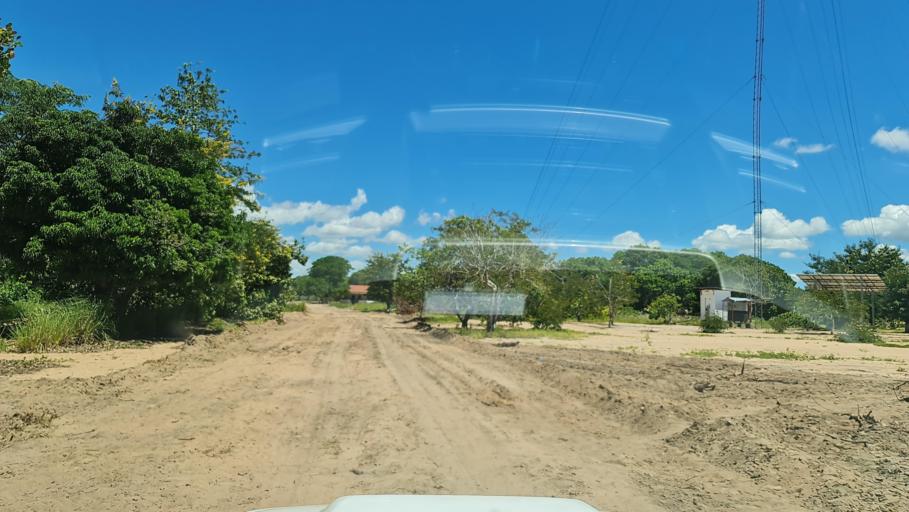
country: MZ
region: Nampula
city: Nampula
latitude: -15.3012
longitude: 39.8718
